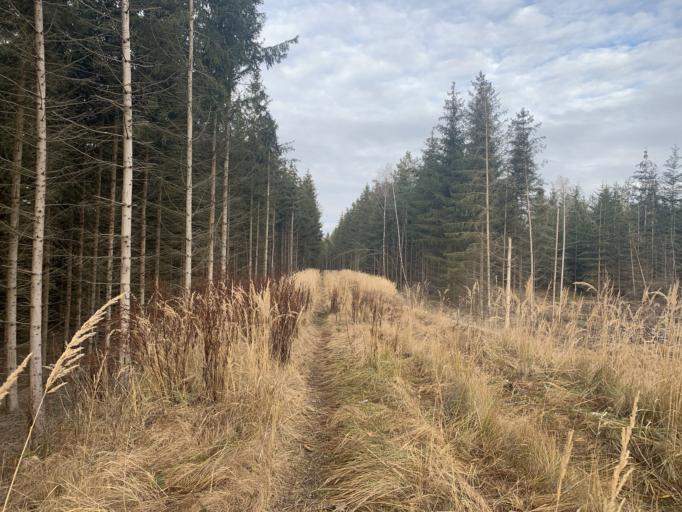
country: CZ
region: Plzensky
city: Zbiroh
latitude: 49.8246
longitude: 13.7935
